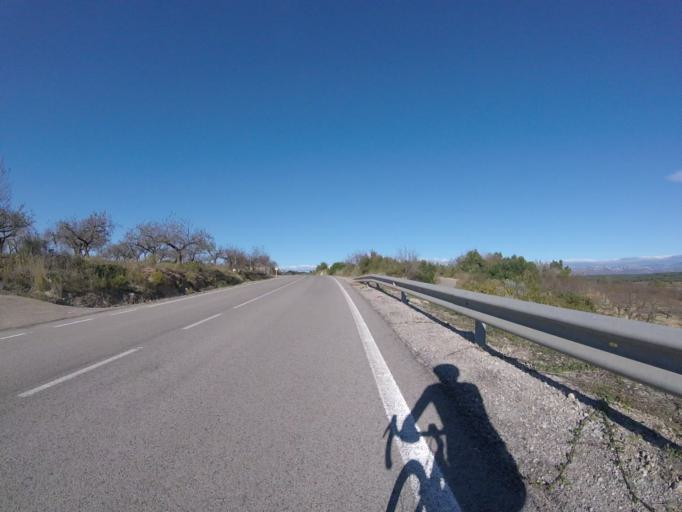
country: ES
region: Valencia
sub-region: Provincia de Castello
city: Cervera del Maestre
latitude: 40.4723
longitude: 0.2394
